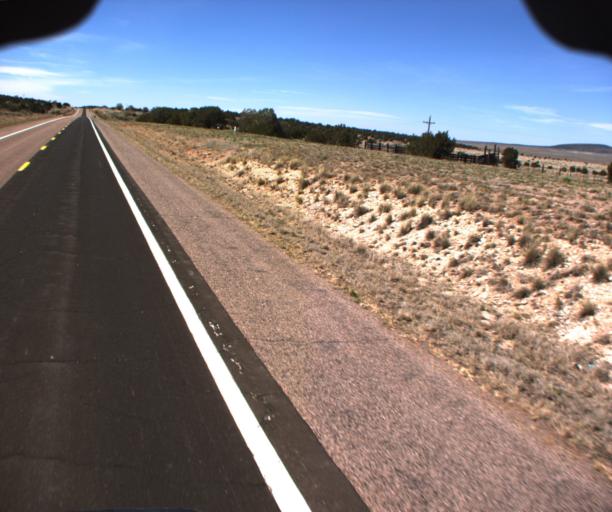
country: US
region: Arizona
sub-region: Mohave County
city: Peach Springs
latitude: 35.5158
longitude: -113.1972
